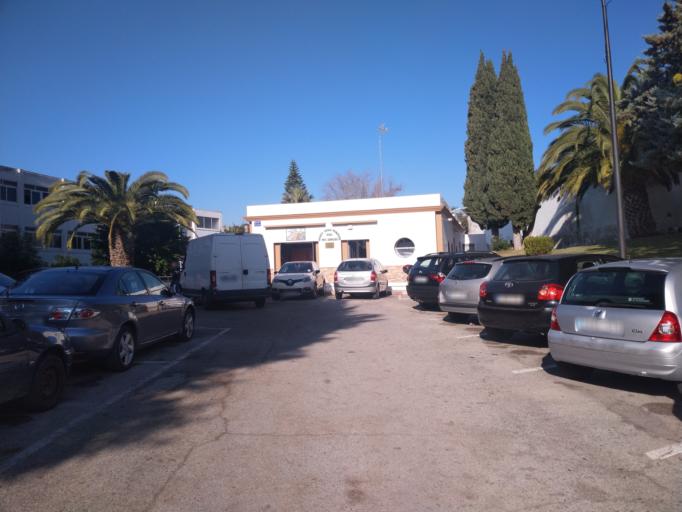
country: ES
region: Andalusia
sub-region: Provincia de Cadiz
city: San Fernando
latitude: 36.4686
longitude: -6.2040
